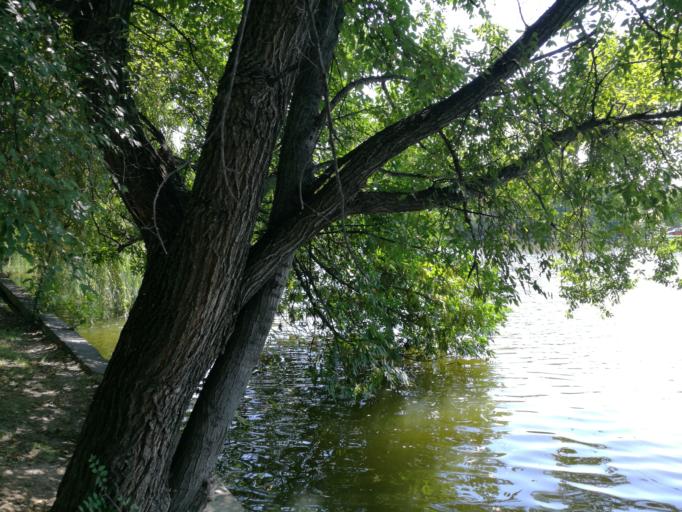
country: RO
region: Bucuresti
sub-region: Municipiul Bucuresti
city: Bucharest
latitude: 44.4885
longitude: 26.0827
